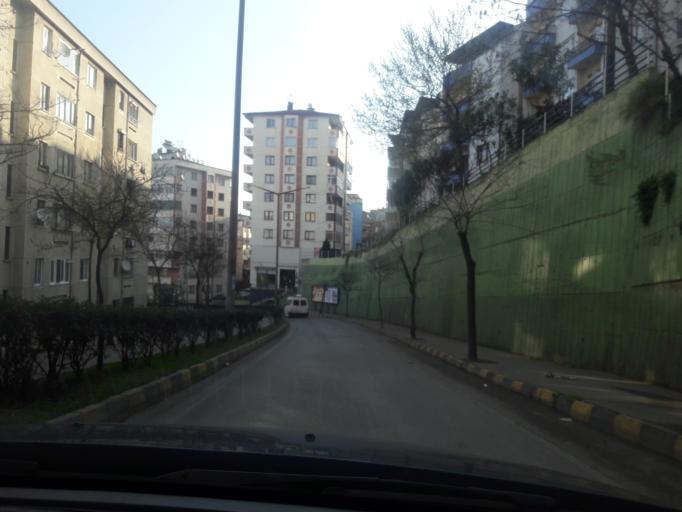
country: TR
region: Trabzon
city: Trabzon
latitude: 40.9966
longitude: 39.6912
